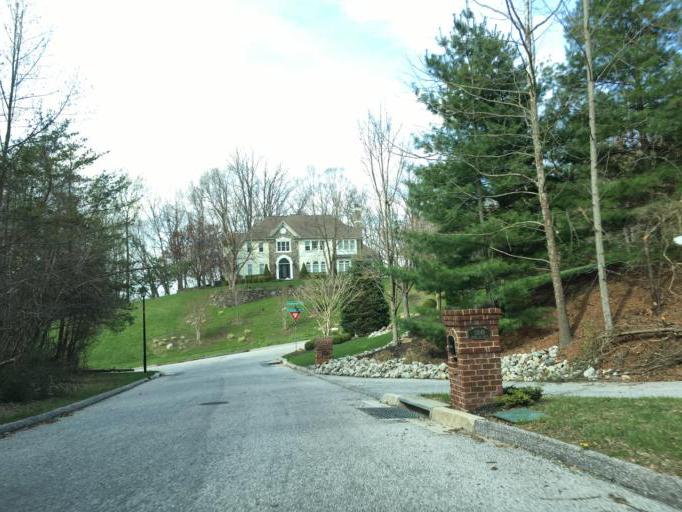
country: US
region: Maryland
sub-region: Baltimore County
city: Cockeysville
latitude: 39.4756
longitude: -76.6736
